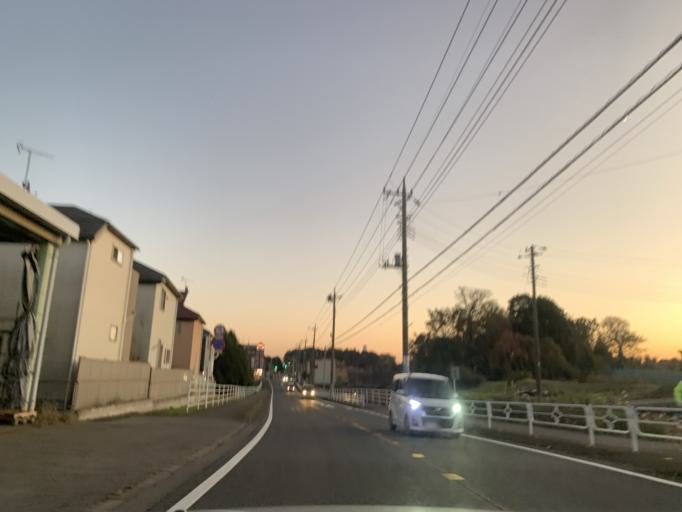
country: JP
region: Chiba
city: Nagareyama
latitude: 35.8938
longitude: 139.9005
